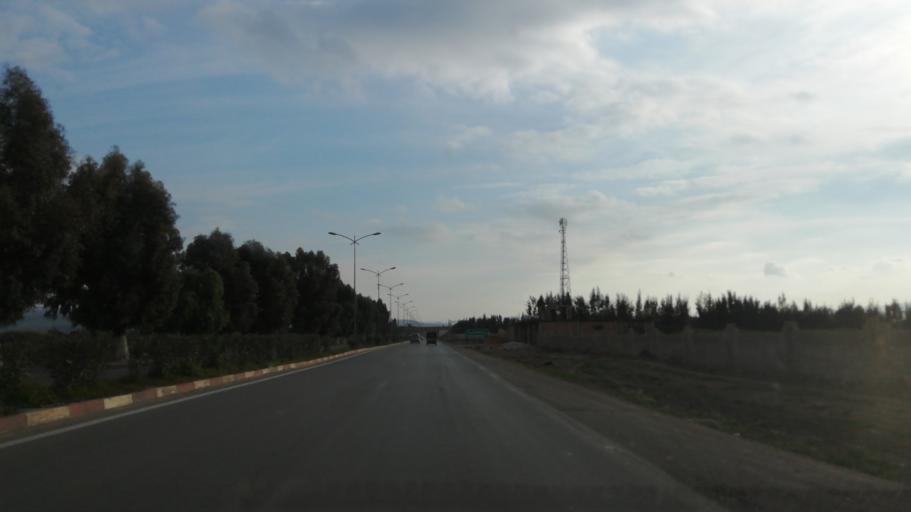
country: DZ
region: Mascara
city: Mascara
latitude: 35.6267
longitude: 0.0615
